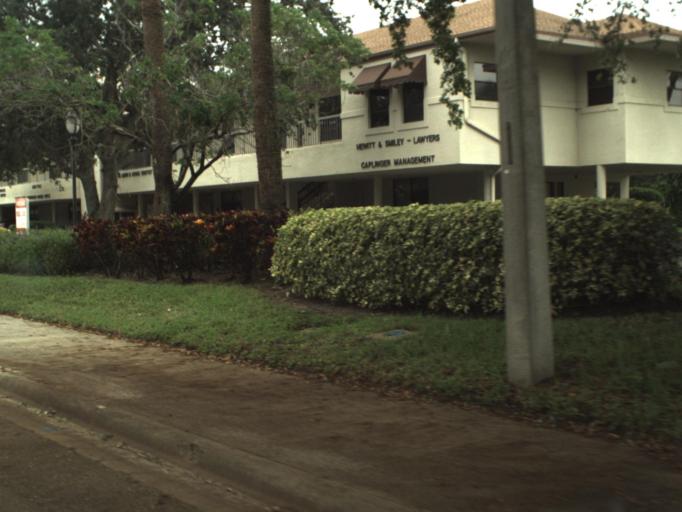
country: US
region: Florida
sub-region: Palm Beach County
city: North Palm Beach
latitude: 26.8334
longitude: -80.1055
